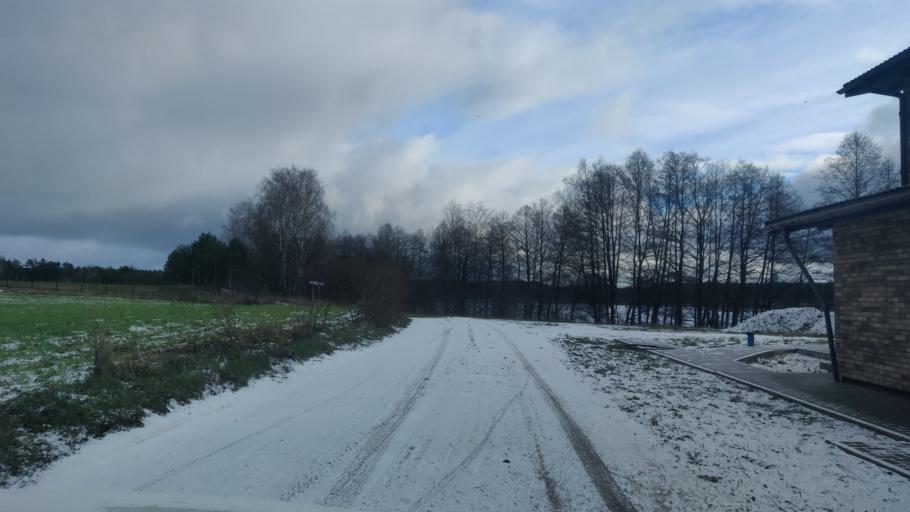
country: LT
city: Trakai
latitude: 54.5538
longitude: 24.9250
